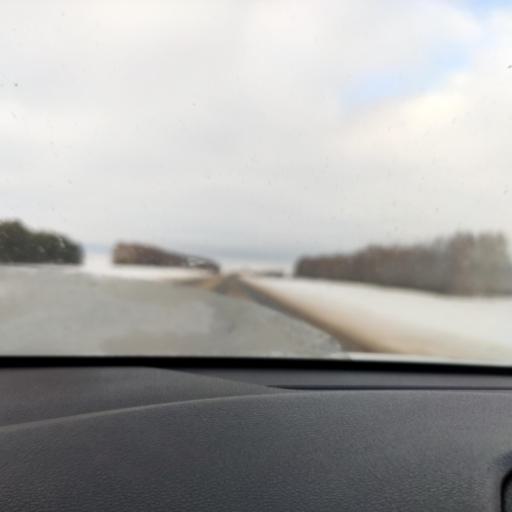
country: RU
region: Tatarstan
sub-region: Arskiy Rayon
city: Arsk
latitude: 56.1687
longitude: 49.9364
